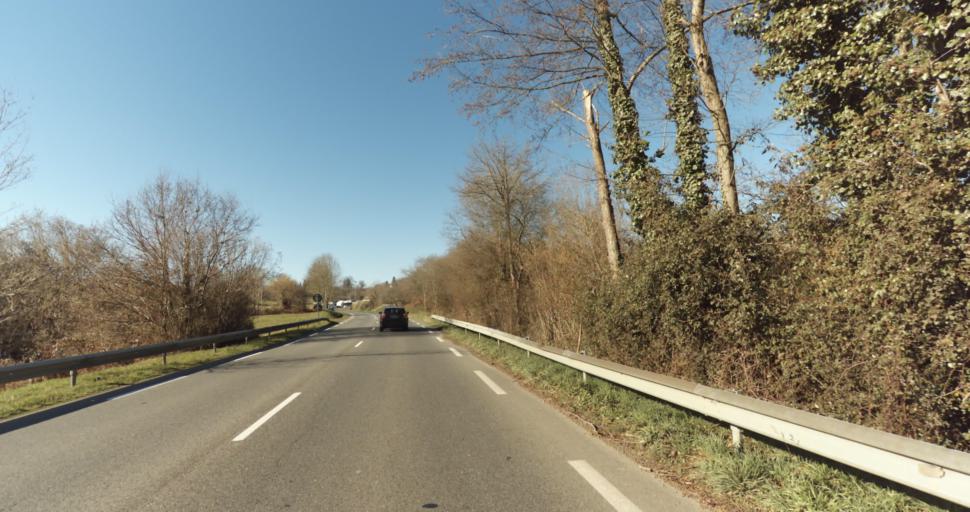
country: FR
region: Aquitaine
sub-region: Departement des Pyrenees-Atlantiques
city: Morlaas
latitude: 43.3383
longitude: -0.2592
